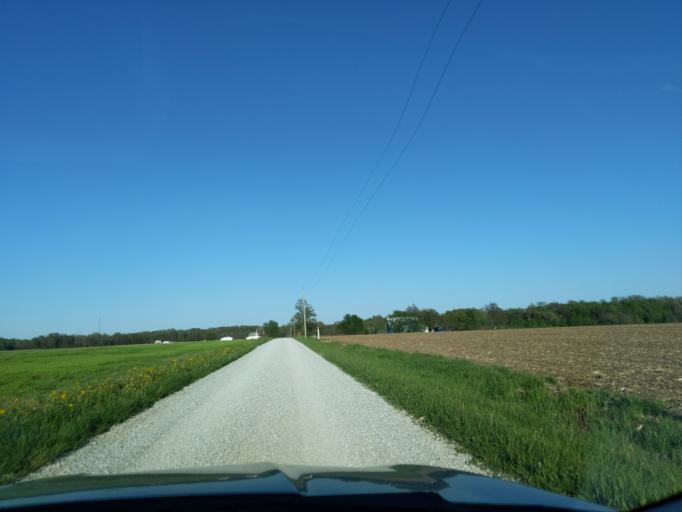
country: US
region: Indiana
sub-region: Decatur County
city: Westport
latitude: 39.1972
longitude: -85.4568
